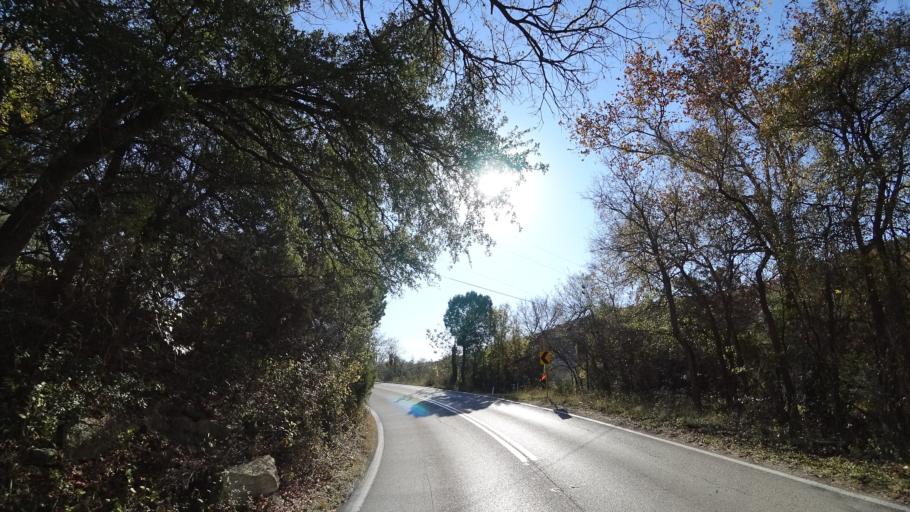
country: US
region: Texas
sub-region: Williamson County
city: Jollyville
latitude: 30.3912
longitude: -97.7784
